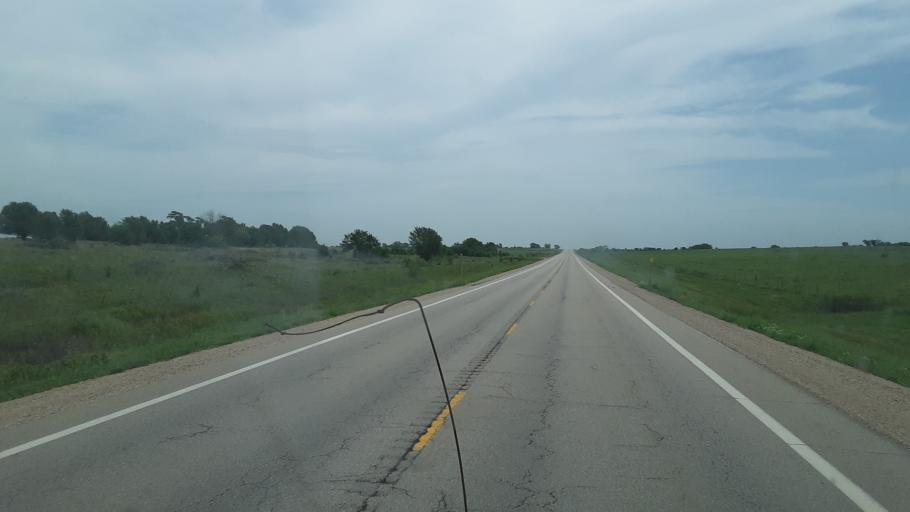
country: US
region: Kansas
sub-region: Woodson County
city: Yates Center
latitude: 37.8362
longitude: -95.9120
